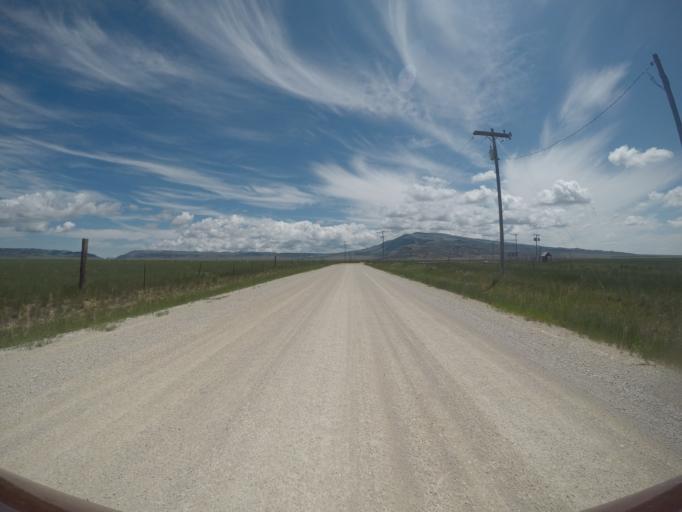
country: US
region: Wyoming
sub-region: Park County
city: Powell
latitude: 45.2051
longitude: -108.7207
